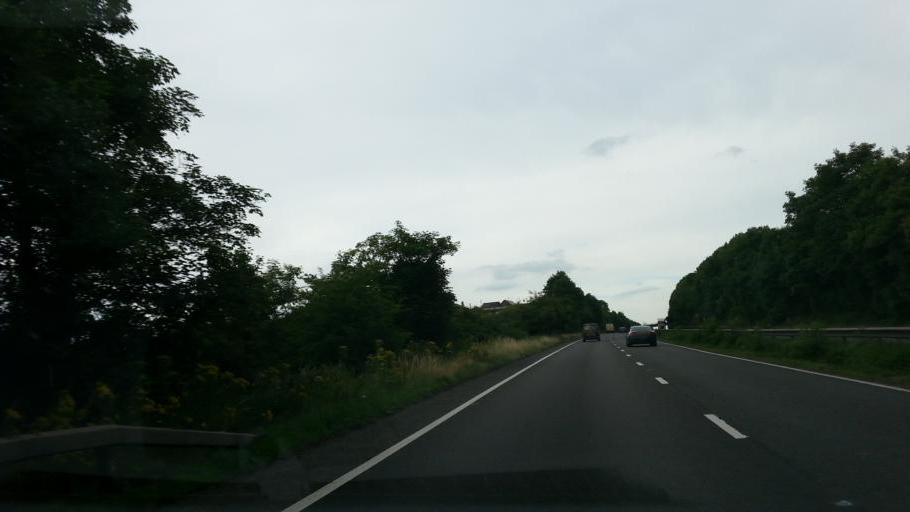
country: GB
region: England
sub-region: Herefordshire
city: Ross on Wye
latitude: 51.9217
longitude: -2.5883
